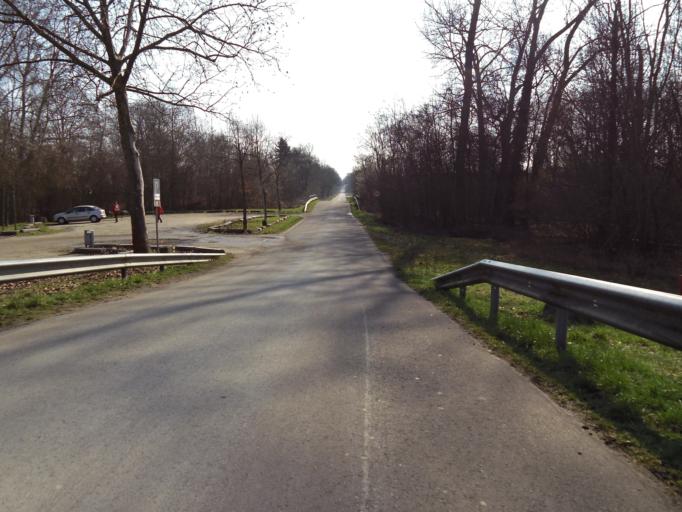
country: DE
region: Rheinland-Pfalz
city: Worms
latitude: 49.6135
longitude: 8.3868
